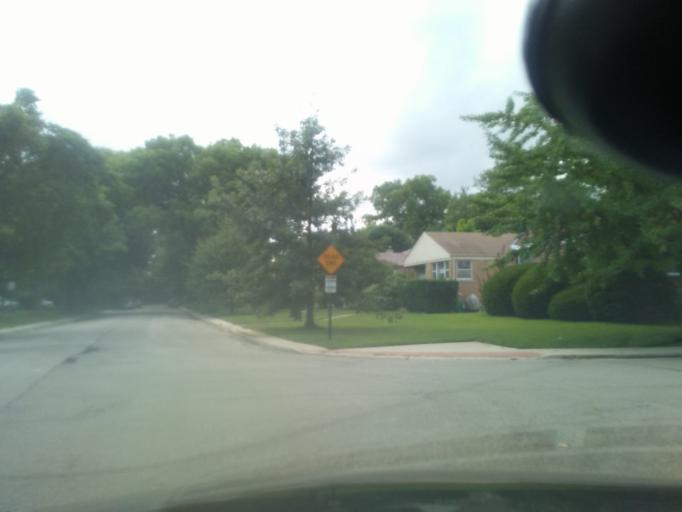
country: US
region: Illinois
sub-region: Cook County
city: Evanston
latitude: 42.0275
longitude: -87.7017
